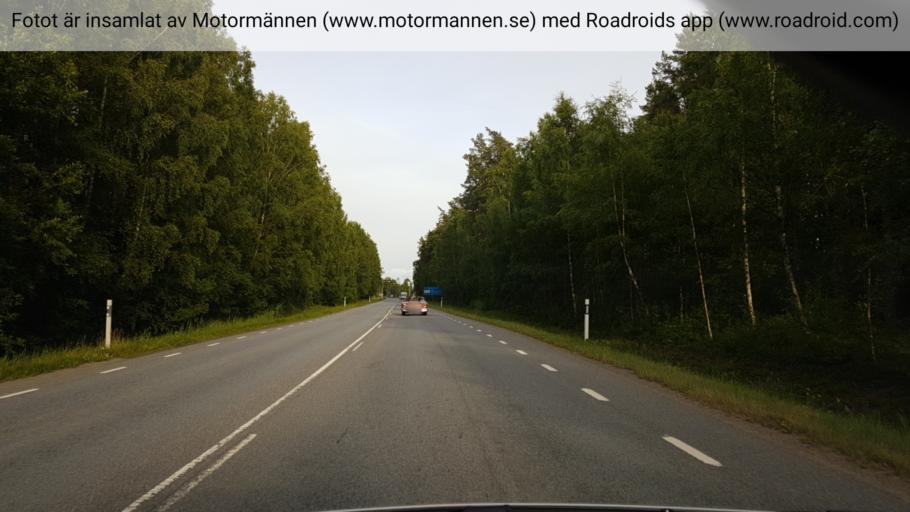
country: SE
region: Vaestra Goetaland
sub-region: Lidkopings Kommun
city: Lidkoping
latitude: 58.4953
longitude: 13.1347
